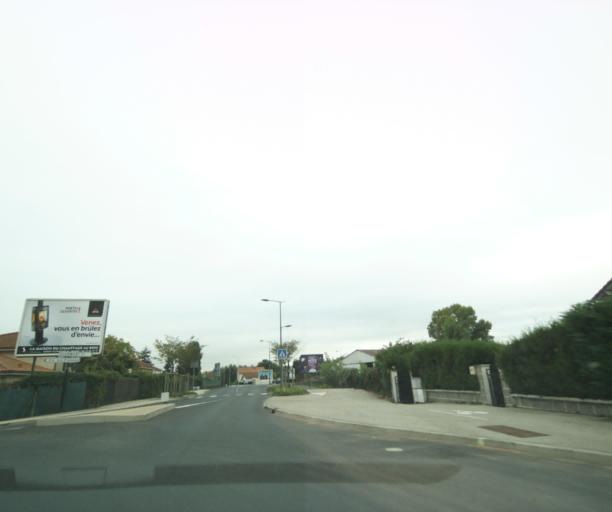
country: FR
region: Auvergne
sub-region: Departement du Puy-de-Dome
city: Gerzat
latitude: 45.8170
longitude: 3.1407
